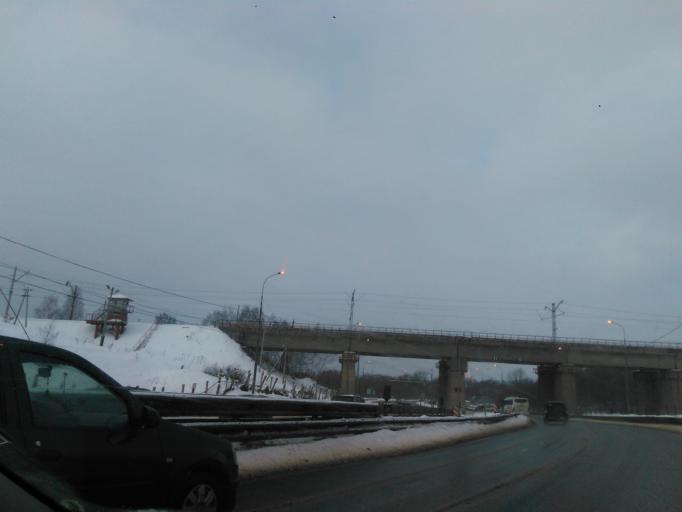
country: RU
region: Moskovskaya
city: Dedenevo
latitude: 56.2579
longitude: 37.5102
